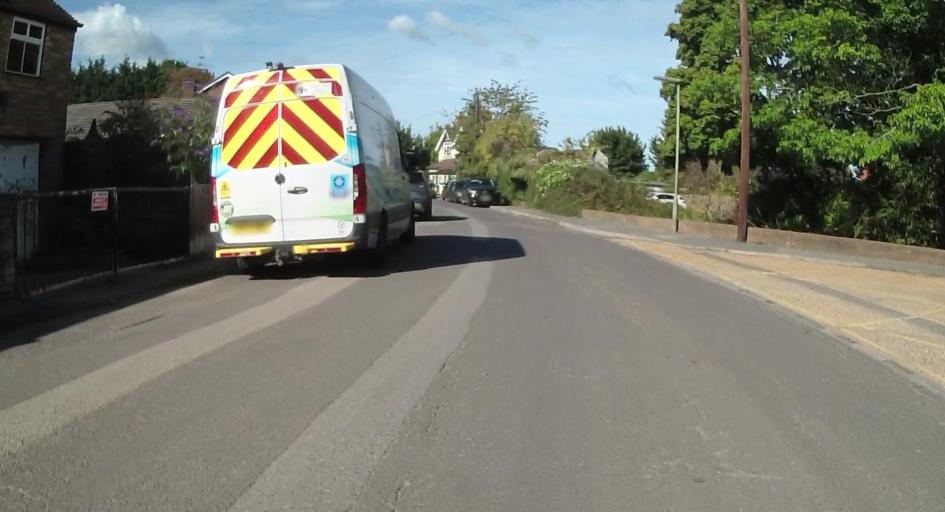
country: GB
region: England
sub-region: Surrey
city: Addlestone
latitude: 51.3812
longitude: -0.4904
